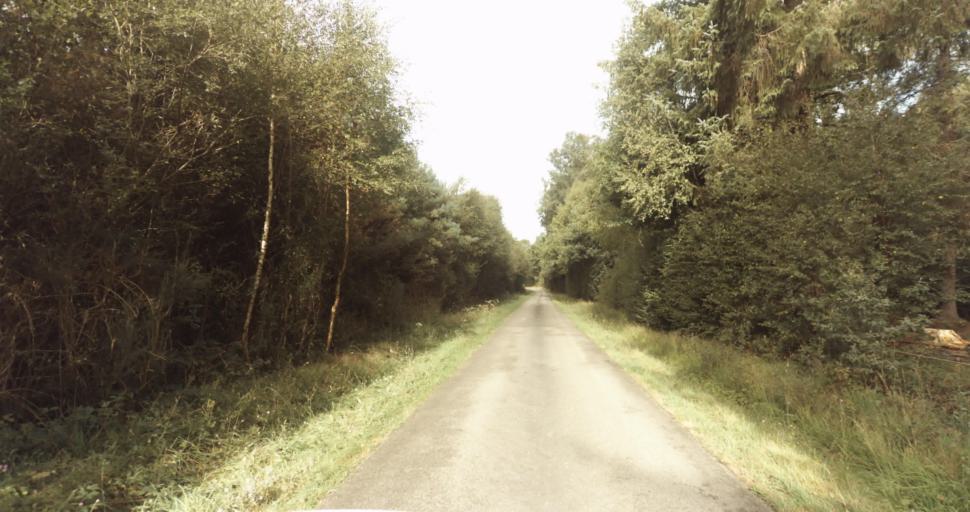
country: FR
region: Lower Normandy
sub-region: Departement de l'Orne
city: Gace
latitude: 48.8585
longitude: 0.3416
